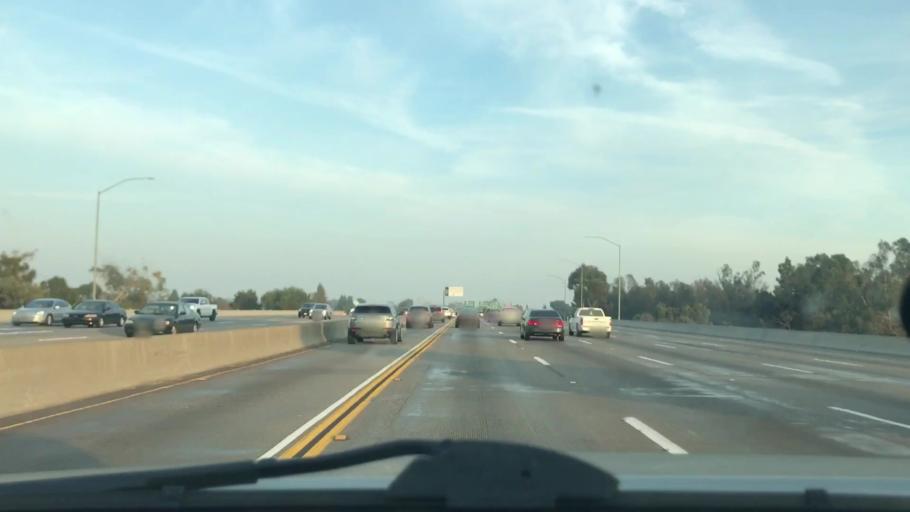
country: US
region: California
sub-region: Los Angeles County
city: Carson
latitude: 33.8256
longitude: -118.2297
